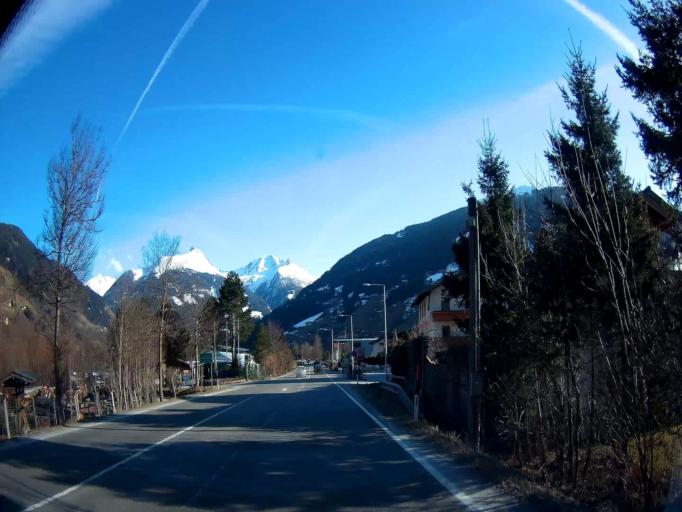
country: AT
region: Salzburg
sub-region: Politischer Bezirk Sankt Johann im Pongau
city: Bad Hofgastein
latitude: 47.1520
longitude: 13.1127
